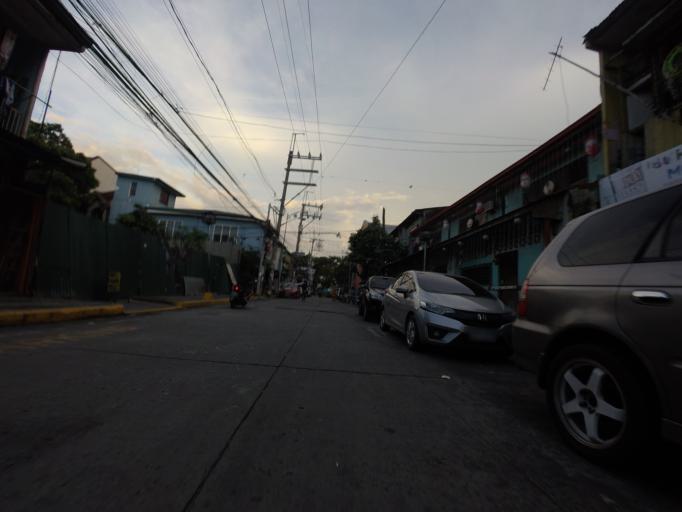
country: PH
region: Metro Manila
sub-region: City of Manila
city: Quiapo
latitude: 14.5926
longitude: 120.9902
